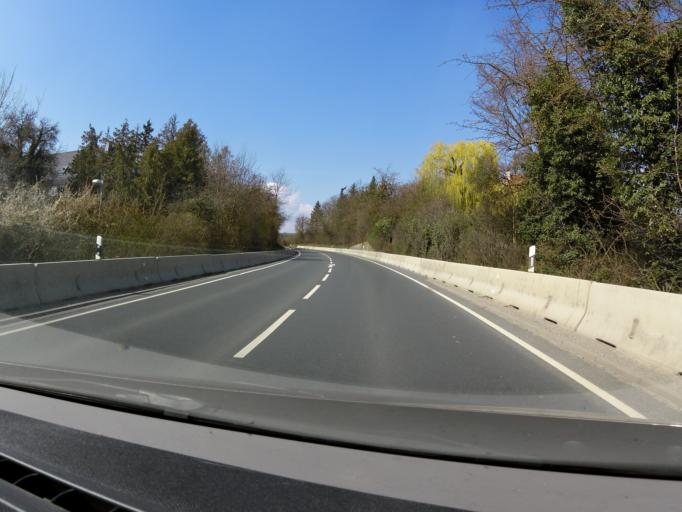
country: DE
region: Bavaria
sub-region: Regierungsbezirk Unterfranken
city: Dettelbach
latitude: 49.8015
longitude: 10.1559
